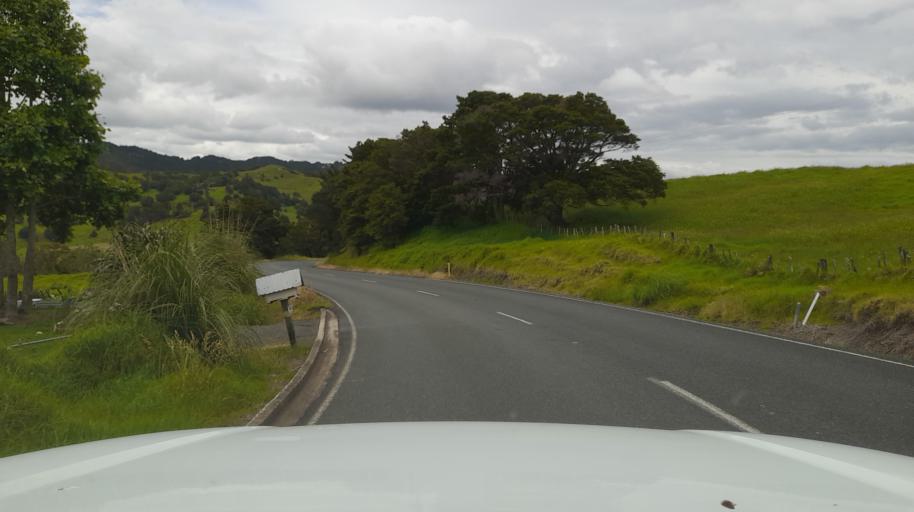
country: NZ
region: Northland
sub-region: Far North District
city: Kaitaia
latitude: -35.3573
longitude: 173.4948
